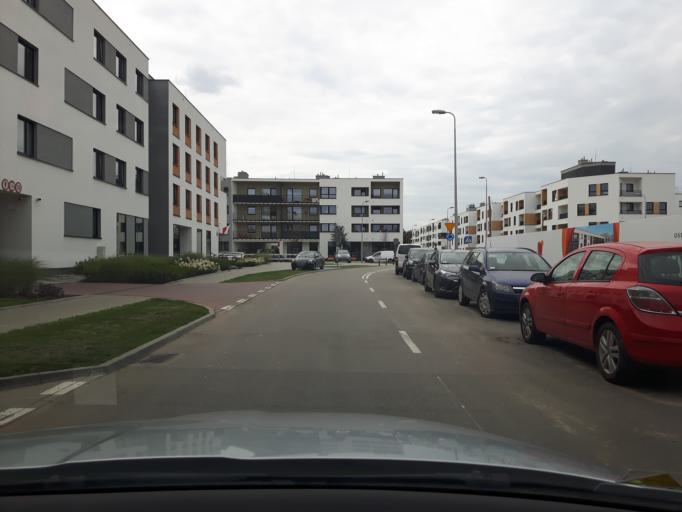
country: PL
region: Masovian Voivodeship
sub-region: Powiat wolominski
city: Zabki
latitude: 52.2779
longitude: 21.0870
